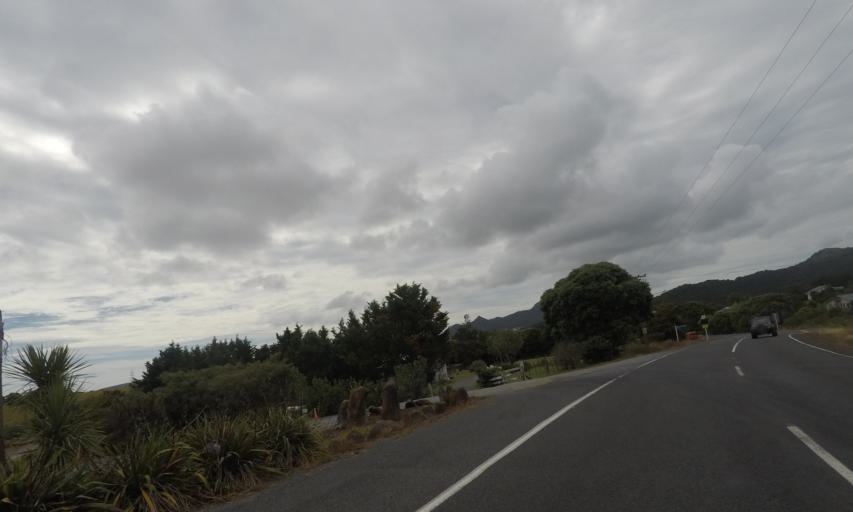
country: NZ
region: Northland
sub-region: Whangarei
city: Ruakaka
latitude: -35.7681
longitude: 174.4770
